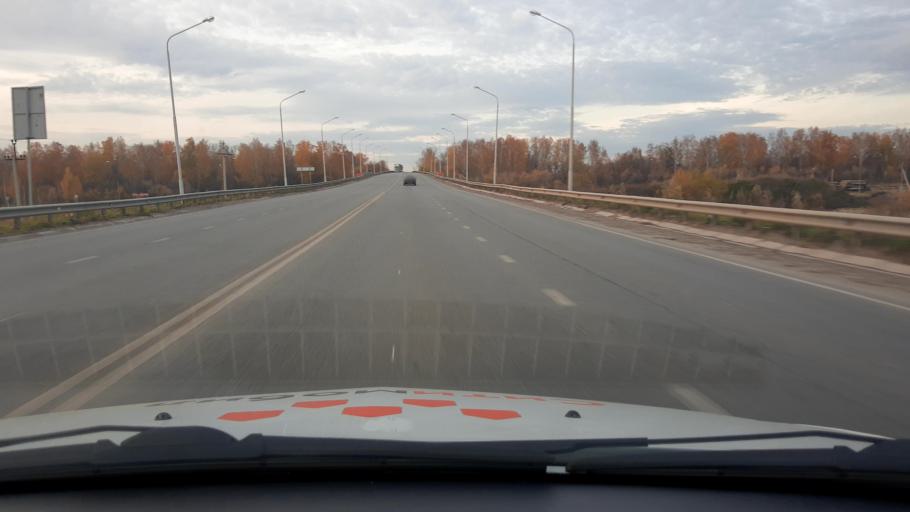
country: RU
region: Bashkortostan
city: Iglino
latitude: 54.7705
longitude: 56.2593
